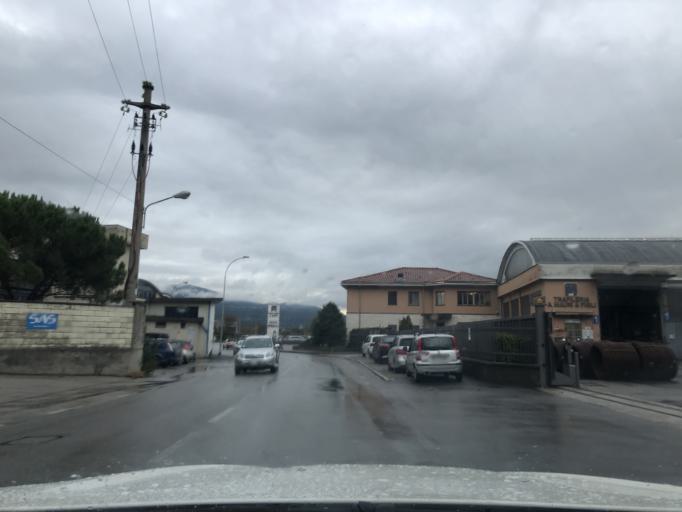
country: IT
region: Lombardy
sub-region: Provincia di Lecco
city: Suello
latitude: 45.8159
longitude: 9.3081
